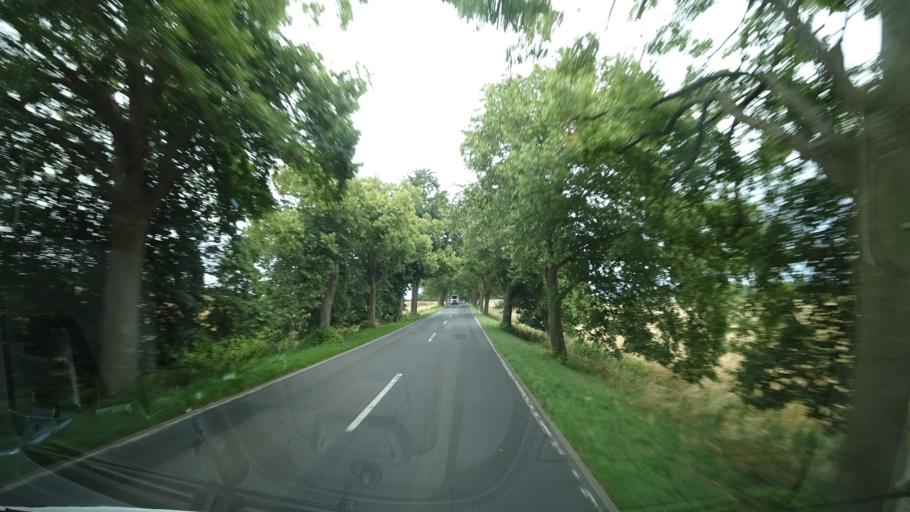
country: DE
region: Mecklenburg-Vorpommern
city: Sehlen
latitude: 54.3331
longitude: 13.3977
